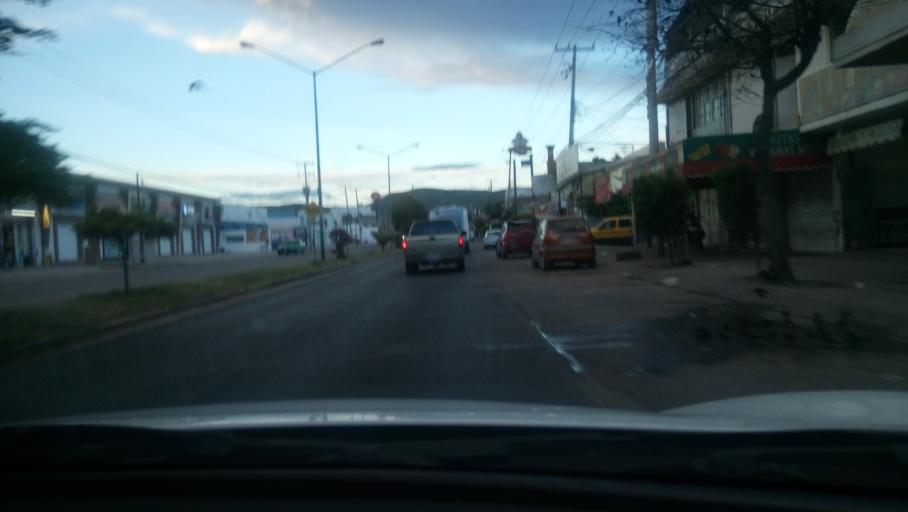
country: MX
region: Guanajuato
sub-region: Leon
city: Medina
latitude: 21.1577
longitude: -101.6511
